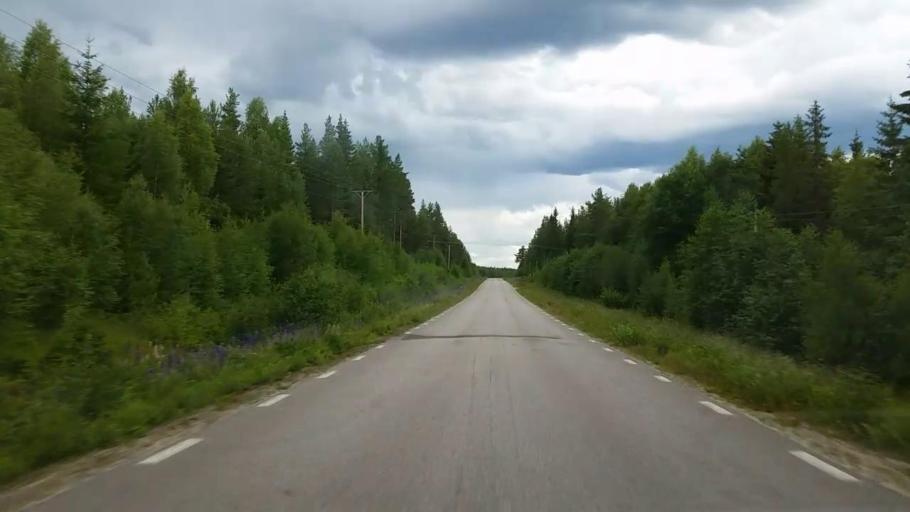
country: SE
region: Gaevleborg
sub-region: Ovanakers Kommun
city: Edsbyn
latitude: 61.4655
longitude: 15.8689
